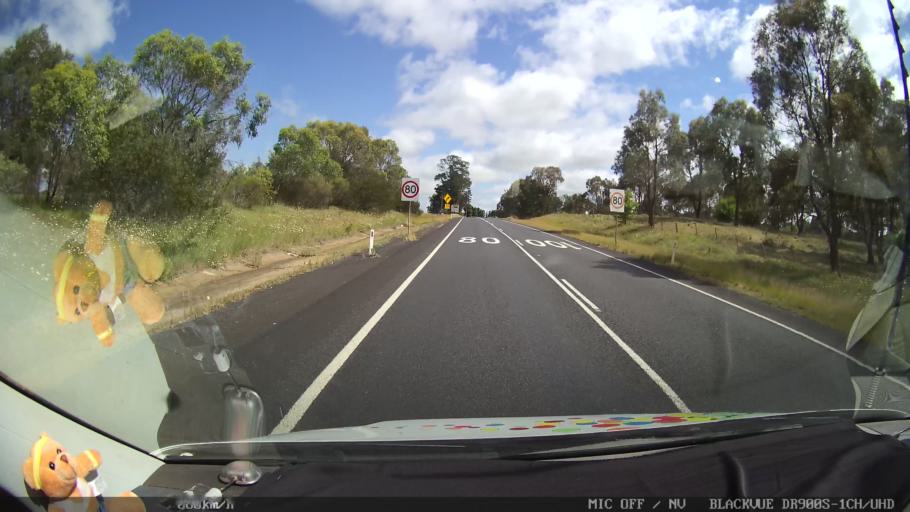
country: AU
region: New South Wales
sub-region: Glen Innes Severn
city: Glen Innes
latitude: -29.9331
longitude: 151.7239
